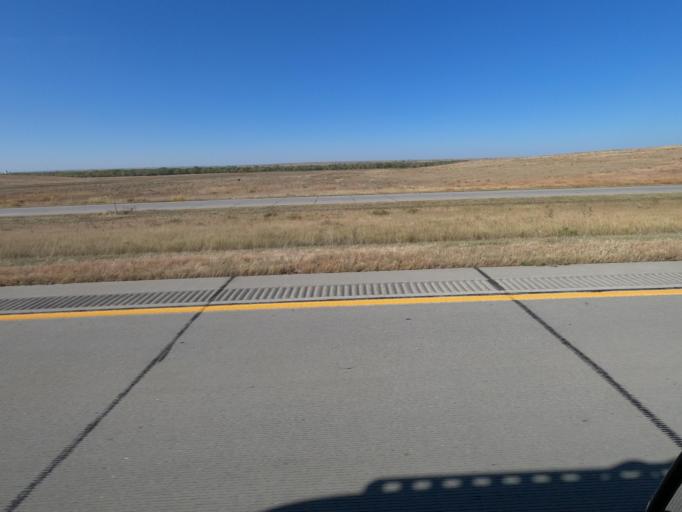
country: US
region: Colorado
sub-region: Sedgwick County
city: Julesburg
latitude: 40.9335
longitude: -102.3152
